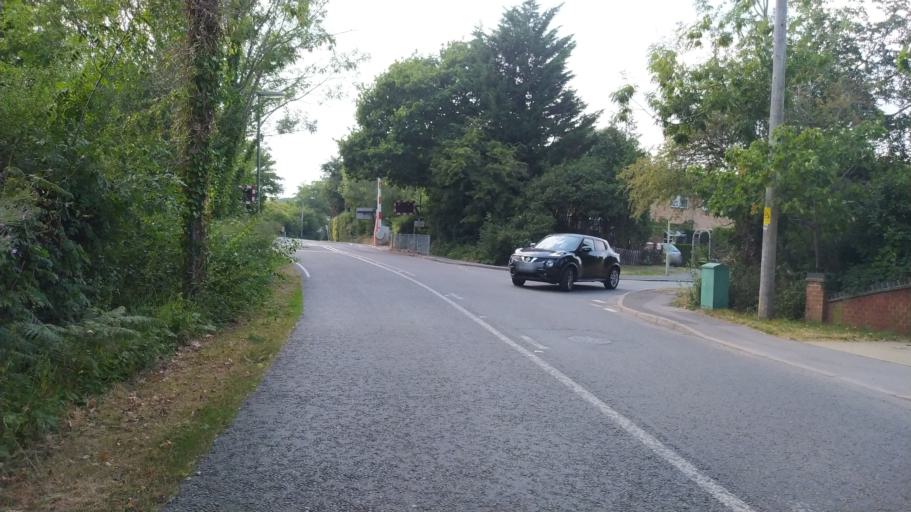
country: GB
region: England
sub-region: Hampshire
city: Totton
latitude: 50.9061
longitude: -1.4908
